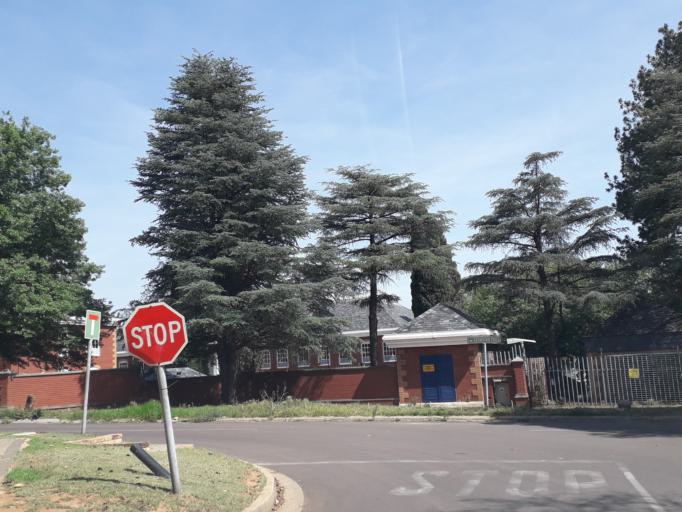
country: ZA
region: Gauteng
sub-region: City of Johannesburg Metropolitan Municipality
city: Diepsloot
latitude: -26.0403
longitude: 28.0171
